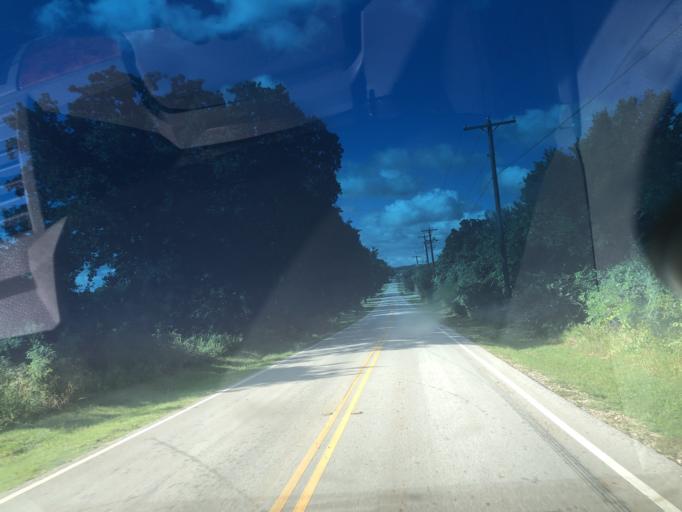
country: US
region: Texas
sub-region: Dallas County
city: Grand Prairie
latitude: 32.7972
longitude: -97.0204
